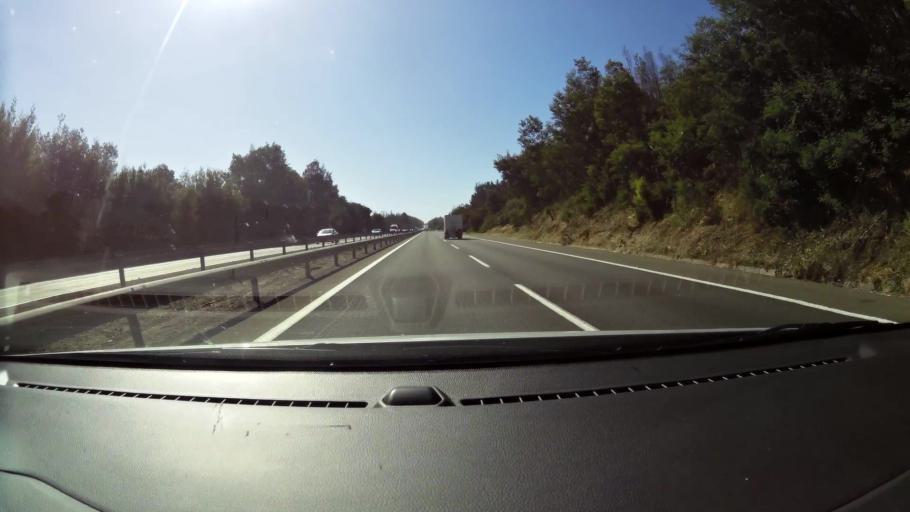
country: CL
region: Valparaiso
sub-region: Provincia de Marga Marga
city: Quilpue
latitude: -33.1766
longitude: -71.5118
